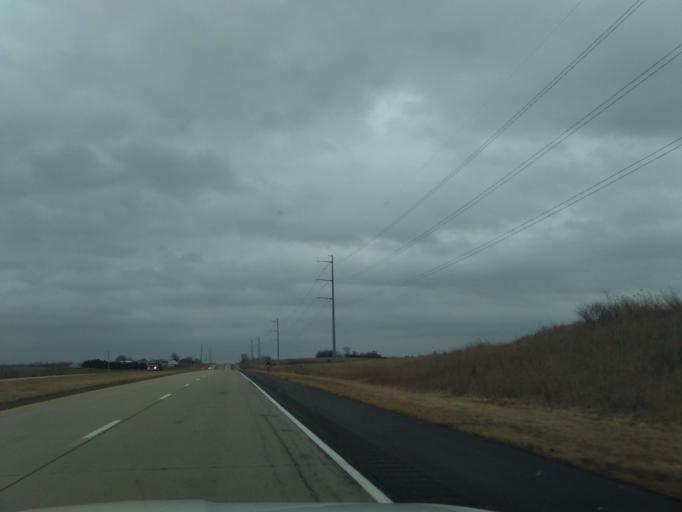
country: US
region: Nebraska
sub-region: Otoe County
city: Syracuse
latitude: 40.6682
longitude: -96.1382
